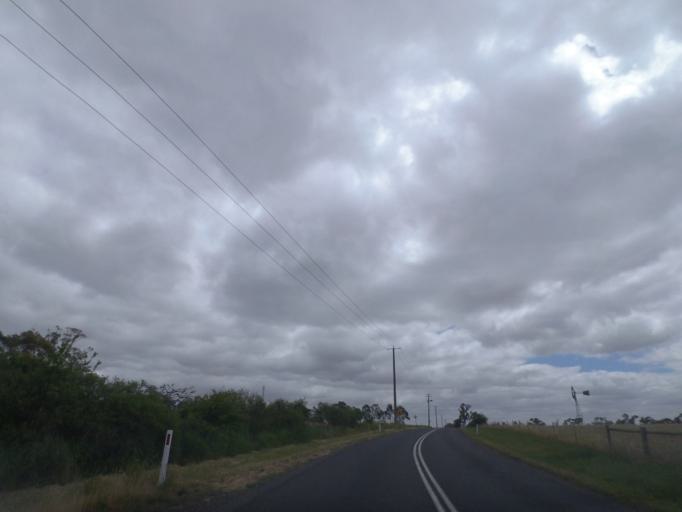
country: AU
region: Victoria
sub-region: Whittlesea
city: Whittlesea
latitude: -37.1876
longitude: 145.0381
